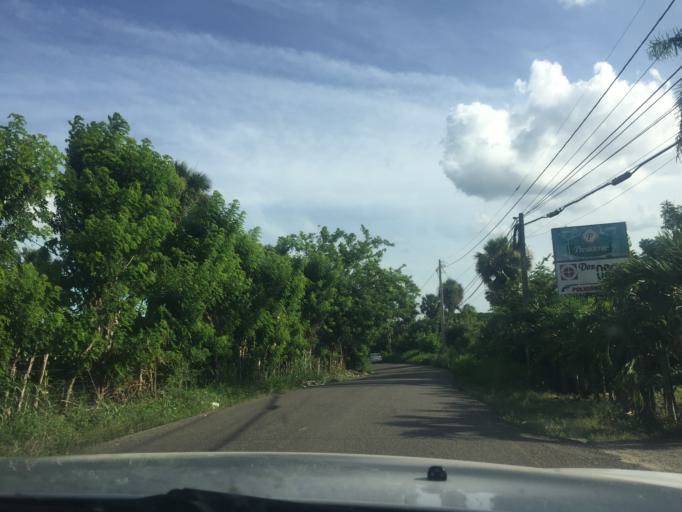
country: DO
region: Santiago
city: Tamboril
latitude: 19.4944
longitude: -70.6349
